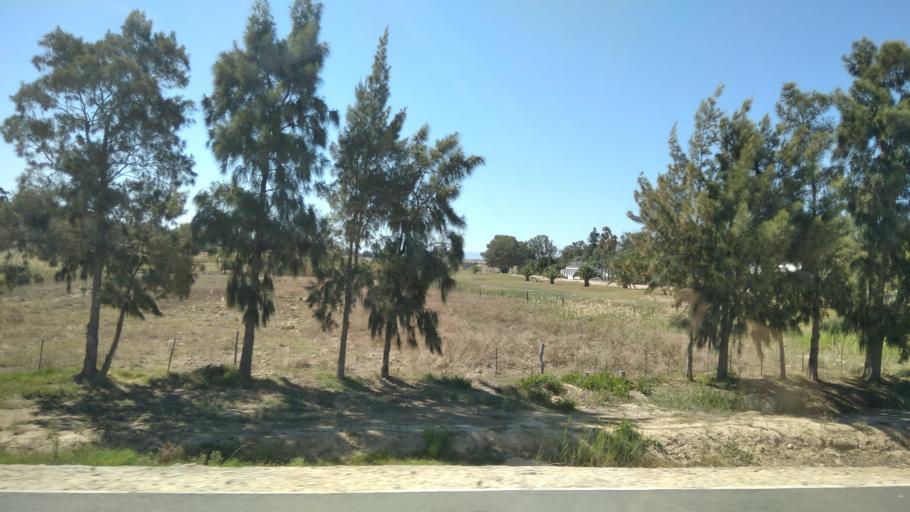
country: ZA
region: Western Cape
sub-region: West Coast District Municipality
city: Moorreesburg
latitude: -33.0621
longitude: 18.3448
